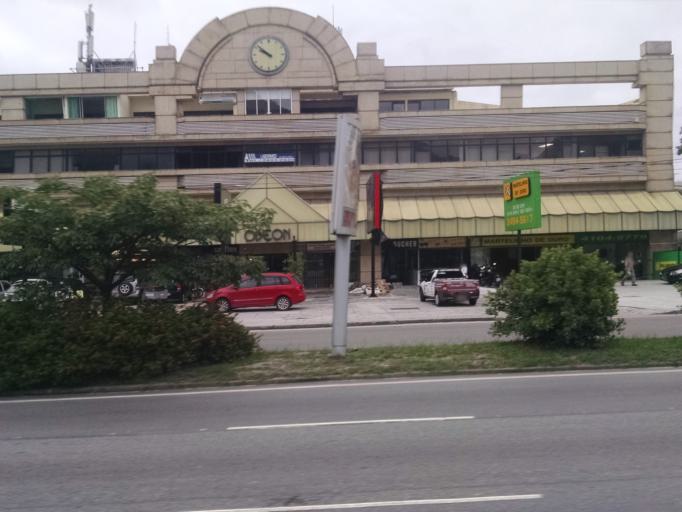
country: BR
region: Rio de Janeiro
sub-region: Rio De Janeiro
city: Rio de Janeiro
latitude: -23.0112
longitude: -43.3009
